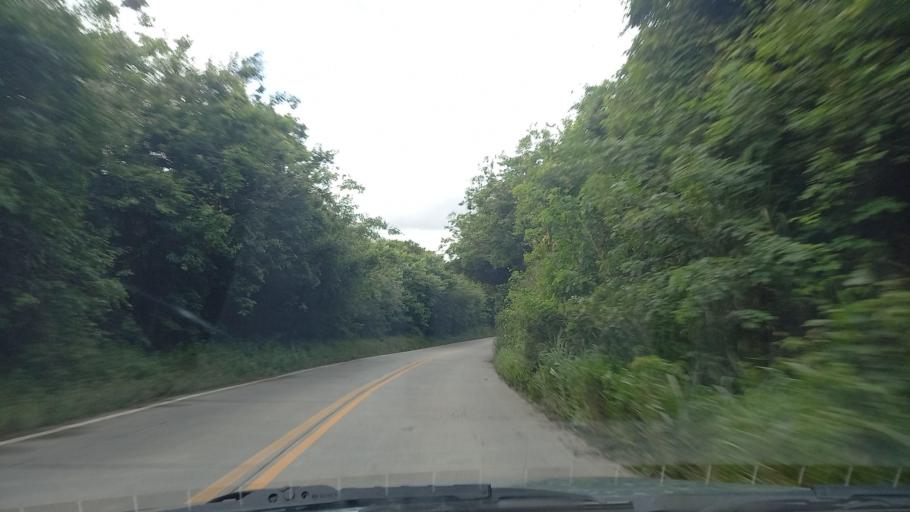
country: BR
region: Pernambuco
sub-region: Quipapa
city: Quipapa
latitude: -8.7818
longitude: -35.9496
